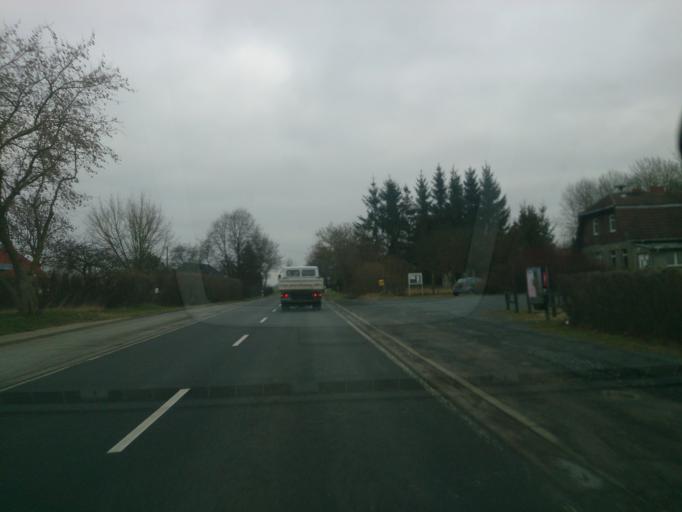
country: DE
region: Mecklenburg-Vorpommern
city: Borrentin
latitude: 53.8245
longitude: 12.9811
